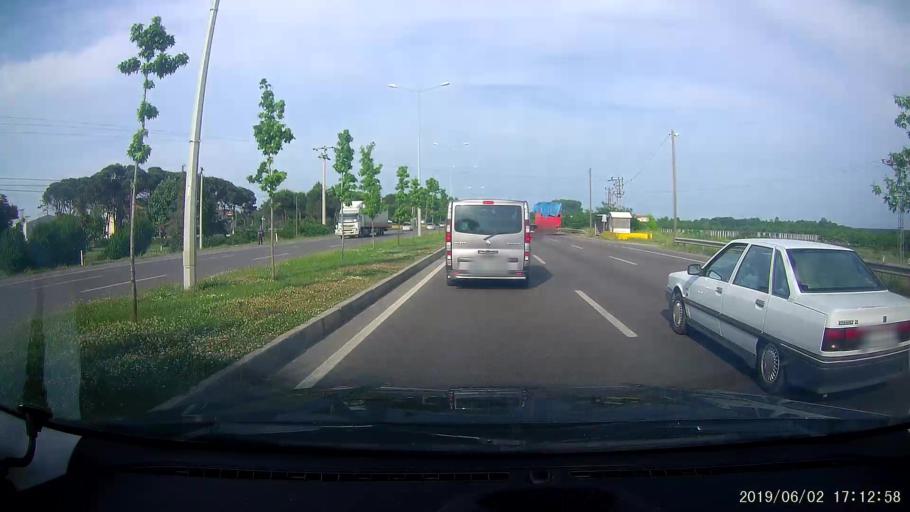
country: TR
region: Samsun
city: Tekkekoy
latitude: 41.2298
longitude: 36.4989
